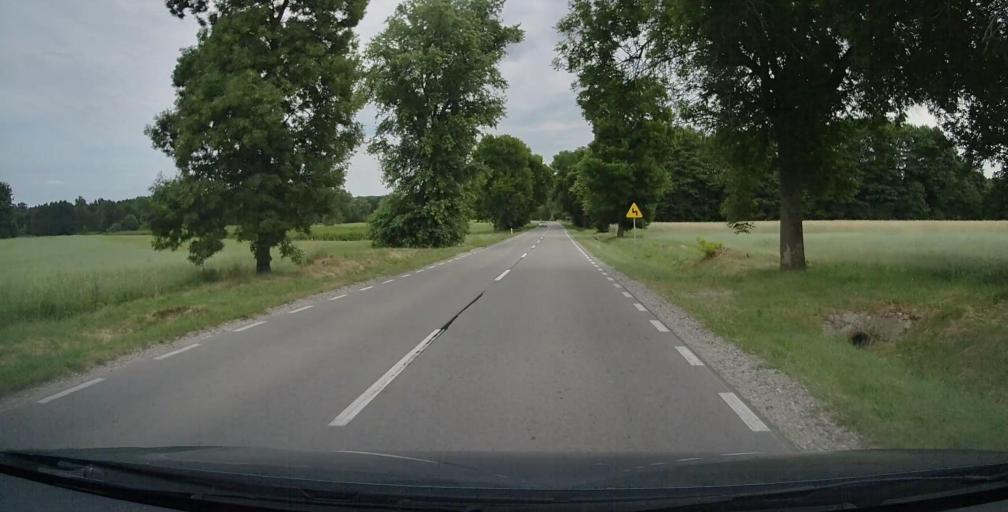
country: PL
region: Masovian Voivodeship
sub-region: Powiat losicki
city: Sarnaki
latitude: 52.3073
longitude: 22.9405
